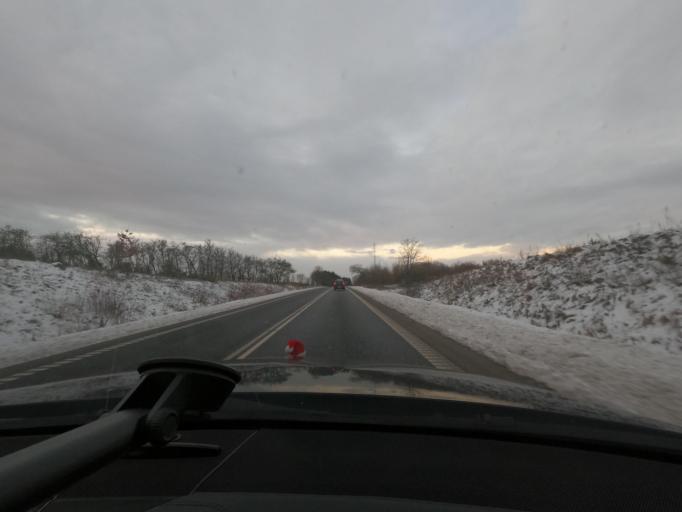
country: DK
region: South Denmark
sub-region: Aabenraa Kommune
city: Krusa
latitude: 54.8632
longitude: 9.4496
